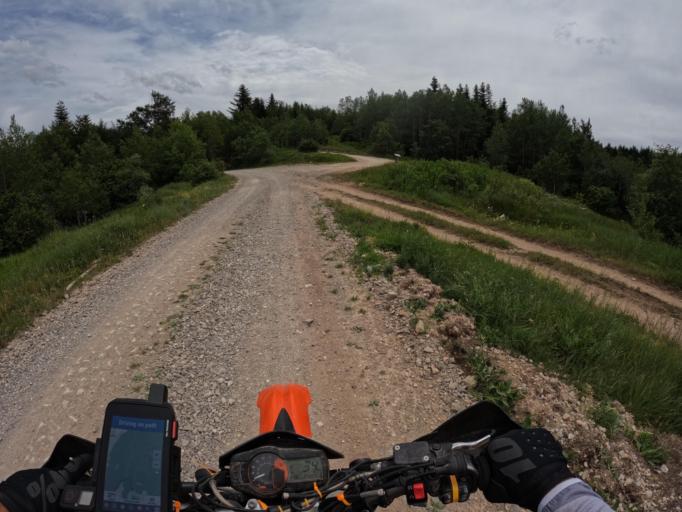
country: BA
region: Federation of Bosnia and Herzegovina
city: Glamoc
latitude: 44.0840
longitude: 16.7292
